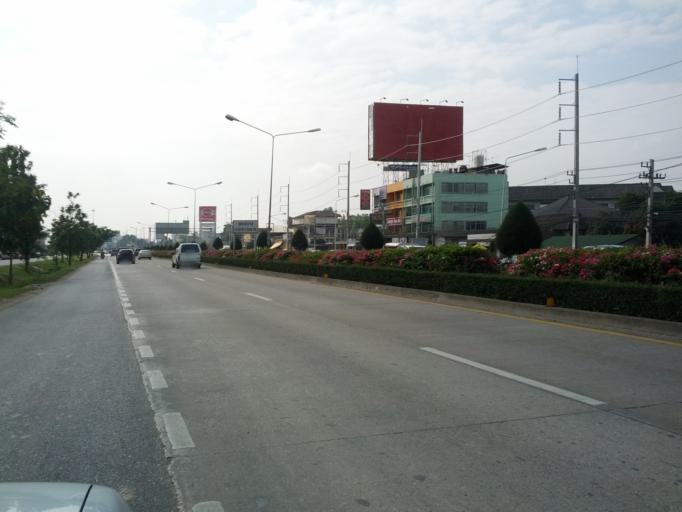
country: TH
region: Chiang Mai
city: Chiang Mai
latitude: 18.7963
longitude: 99.0218
